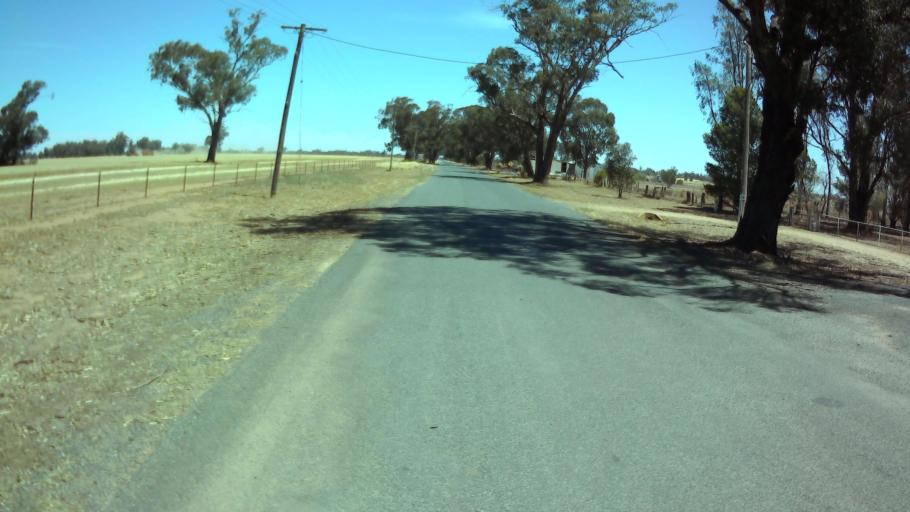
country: AU
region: New South Wales
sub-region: Weddin
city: Grenfell
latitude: -34.0146
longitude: 147.7939
